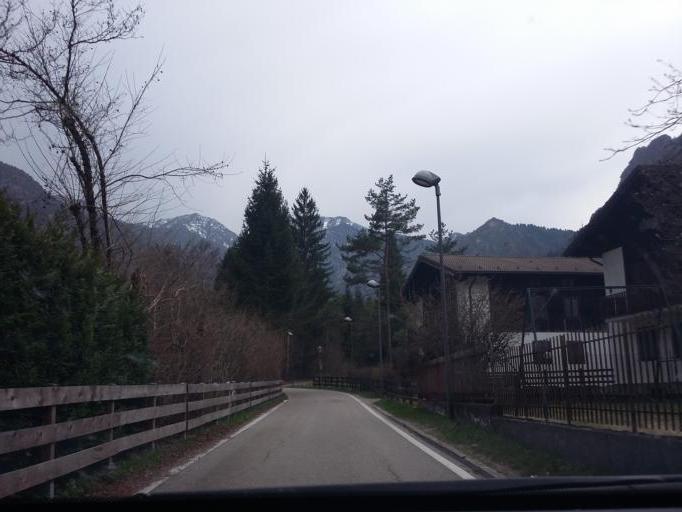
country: IT
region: Trentino-Alto Adige
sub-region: Provincia di Trento
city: Pieve di Ledro
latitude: 45.8680
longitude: 10.7463
